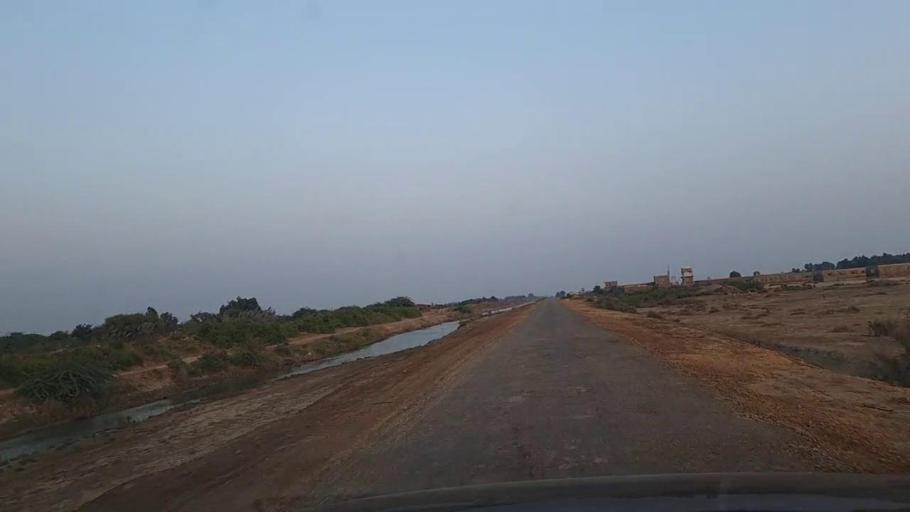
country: PK
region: Sindh
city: Mirpur Sakro
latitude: 24.6354
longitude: 67.6069
